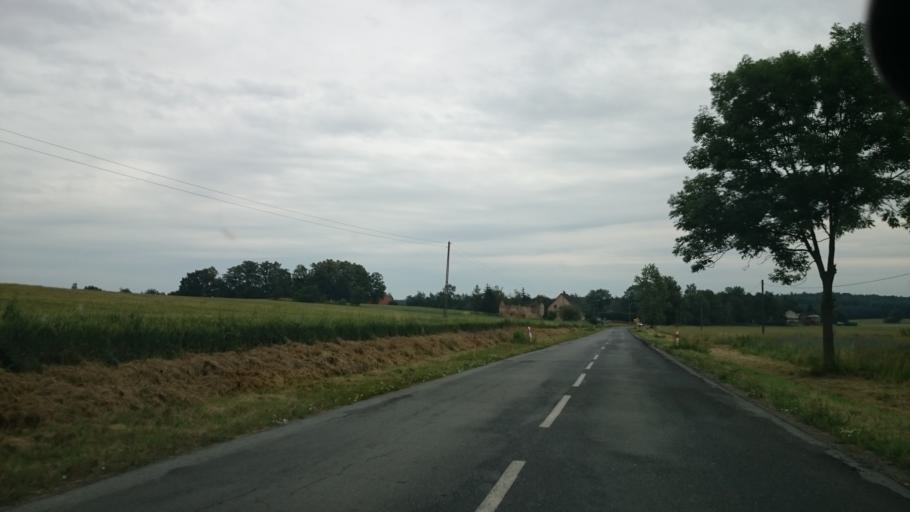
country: PL
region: Lower Silesian Voivodeship
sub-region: Powiat strzelinski
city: Przeworno
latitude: 50.6435
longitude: 17.2201
